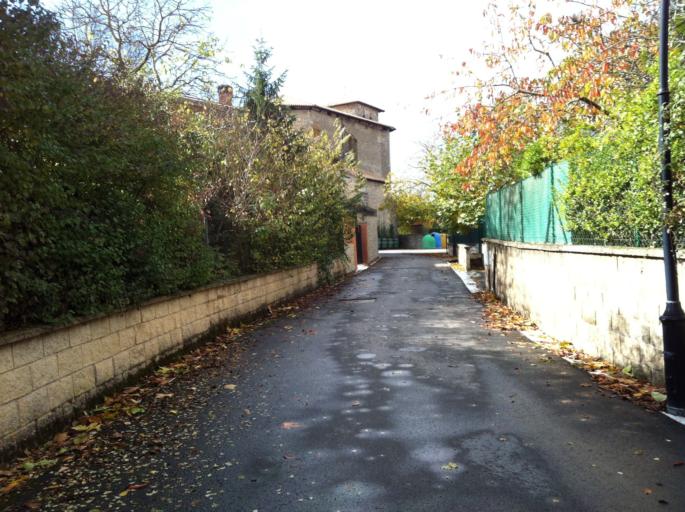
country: ES
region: Basque Country
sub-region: Provincia de Alava
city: Gasteiz / Vitoria
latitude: 42.8195
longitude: -2.6897
